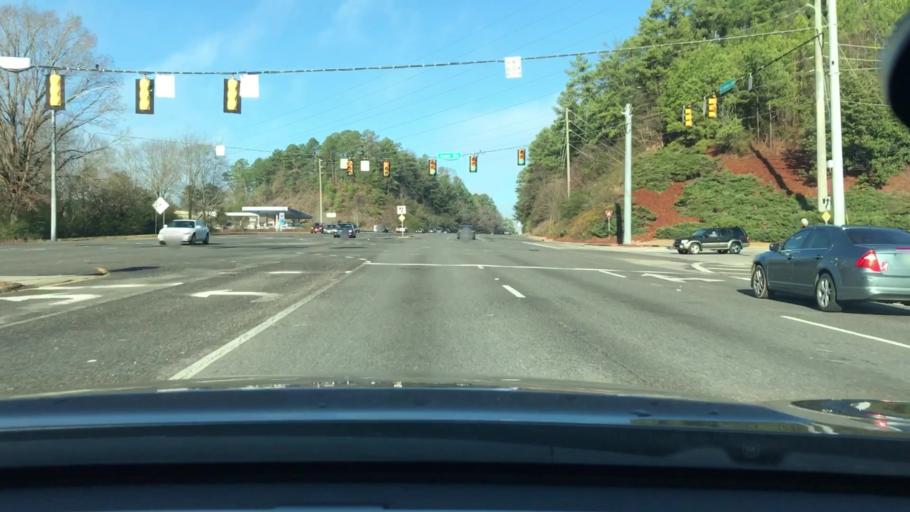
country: US
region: Alabama
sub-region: Jefferson County
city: Cahaba Heights
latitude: 33.4449
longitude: -86.7346
